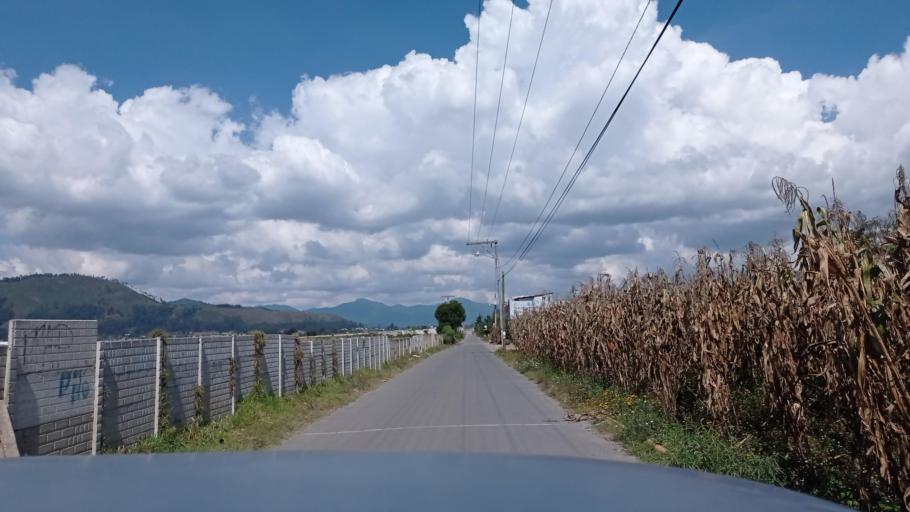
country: GT
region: Quetzaltenango
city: Olintepeque
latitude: 14.8679
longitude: -91.4968
